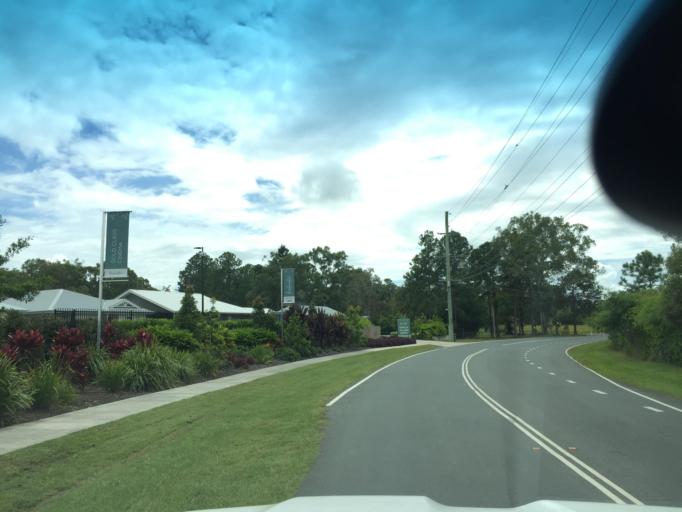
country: AU
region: Queensland
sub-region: Moreton Bay
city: Burpengary
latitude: -27.1691
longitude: 152.9872
